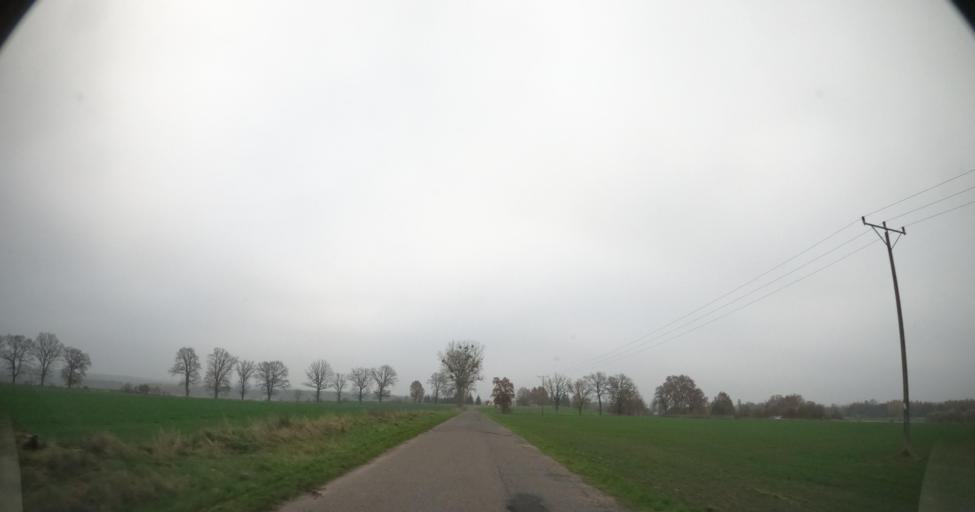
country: PL
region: West Pomeranian Voivodeship
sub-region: Powiat lobeski
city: Wegorzyno
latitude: 53.5407
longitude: 15.6650
